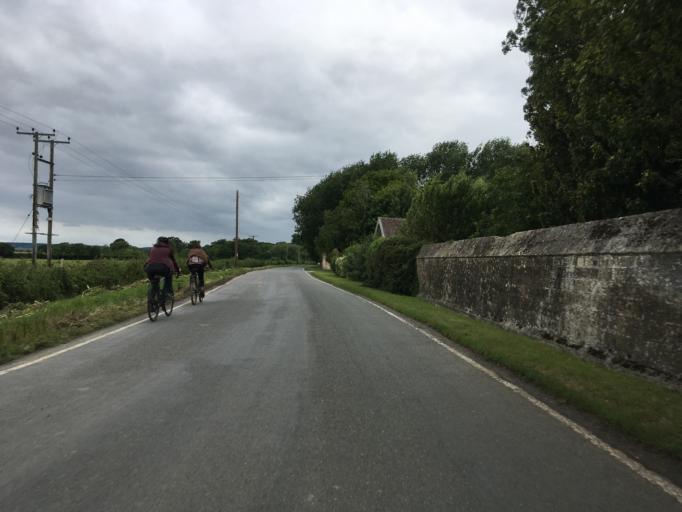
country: GB
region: England
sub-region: Gloucestershire
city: Dursley
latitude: 51.7790
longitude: -2.3814
